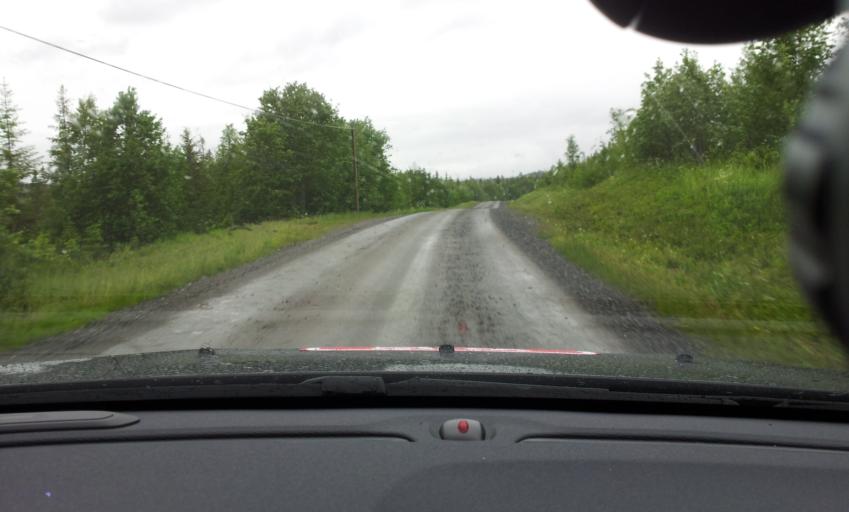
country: SE
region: Jaemtland
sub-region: Are Kommun
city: Are
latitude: 63.4864
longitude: 12.7770
